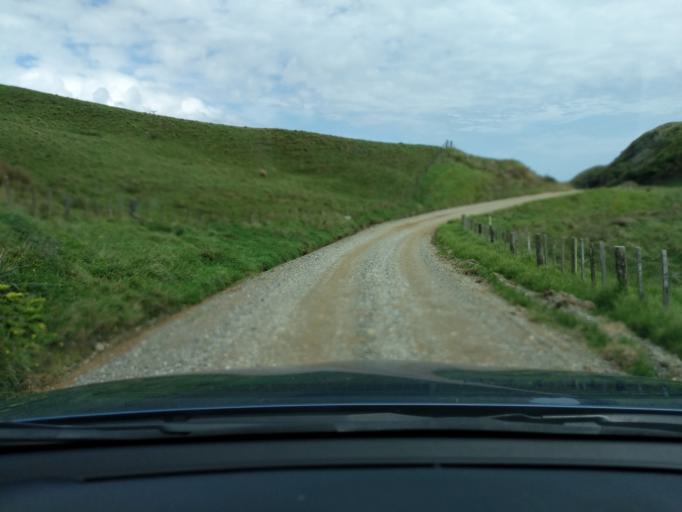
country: NZ
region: Tasman
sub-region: Tasman District
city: Takaka
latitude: -40.6521
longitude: 172.4217
